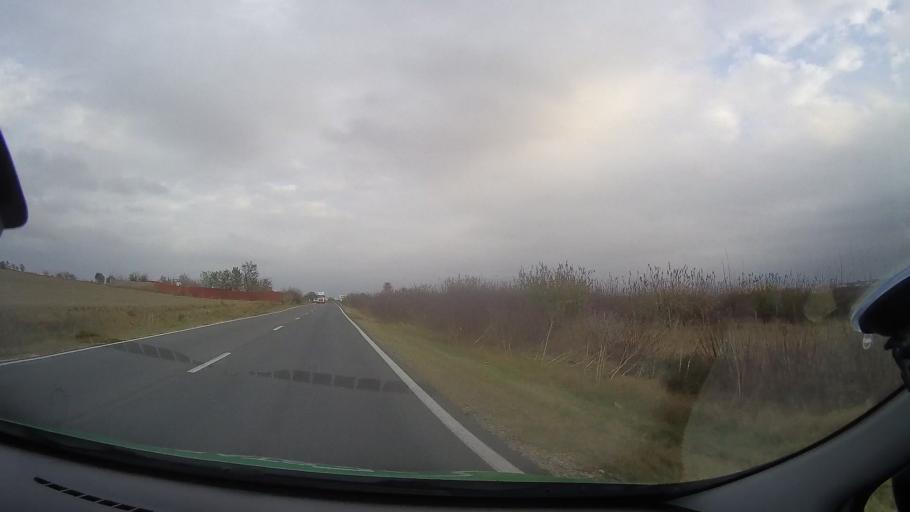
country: RO
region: Constanta
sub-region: Comuna Mircea Voda
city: Satu Nou
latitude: 44.2654
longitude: 28.2451
